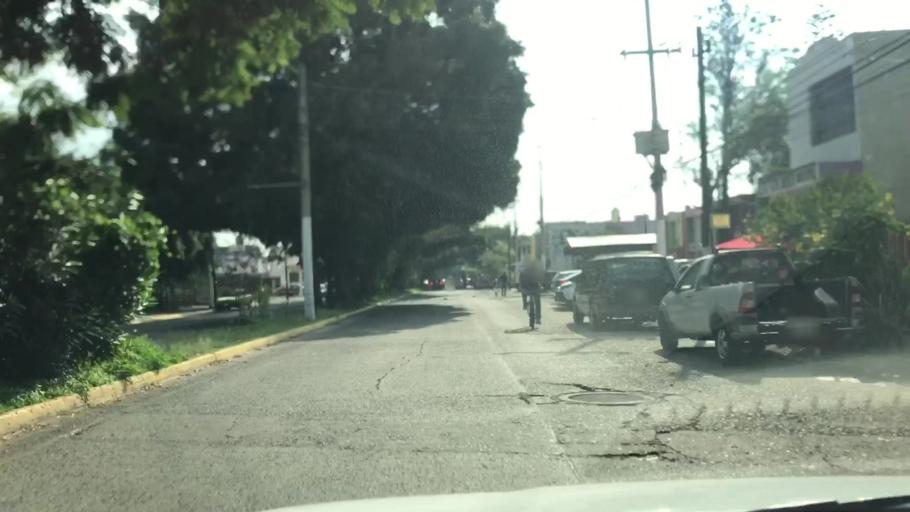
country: MX
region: Jalisco
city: Guadalajara
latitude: 20.6504
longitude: -103.4282
